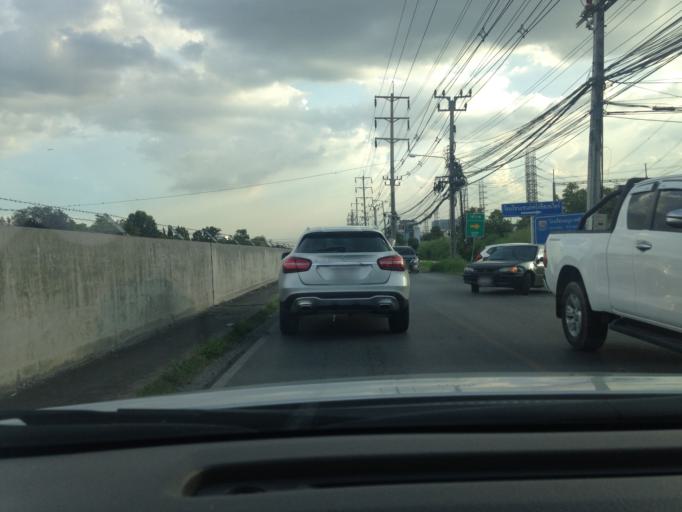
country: TH
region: Bangkok
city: Don Mueang
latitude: 13.9115
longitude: 100.5581
